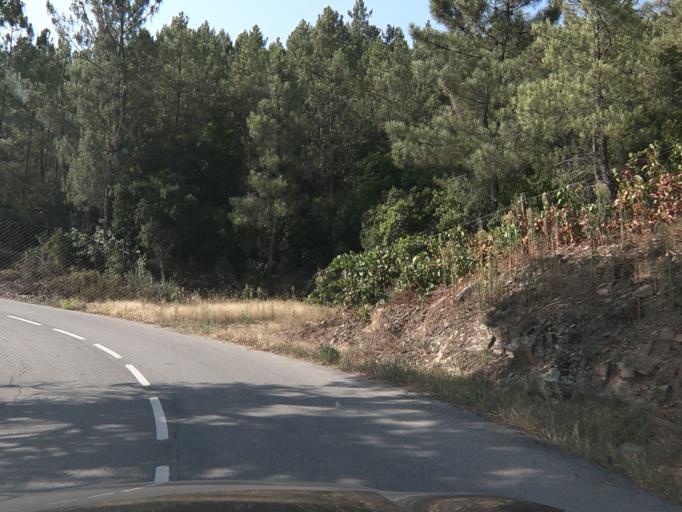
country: PT
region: Vila Real
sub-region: Sabrosa
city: Vilela
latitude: 41.1934
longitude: -7.6320
